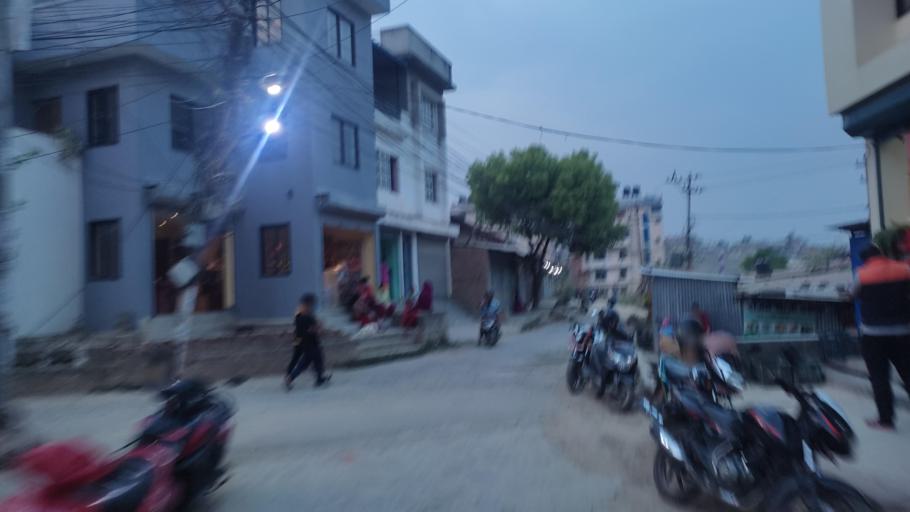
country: NP
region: Central Region
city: Kirtipur
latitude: 27.6714
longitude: 85.2765
